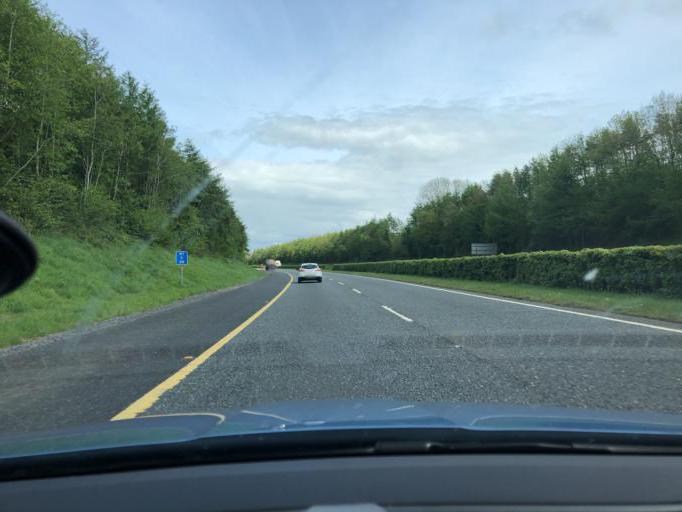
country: IE
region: Leinster
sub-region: Kildare
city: Athgarvan
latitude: 53.1603
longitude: -6.7938
